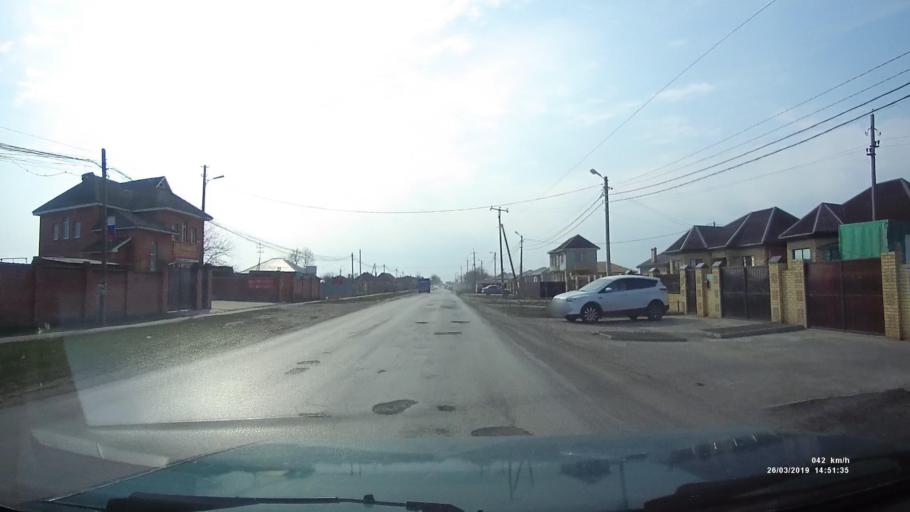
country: RU
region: Rostov
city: Novobessergenovka
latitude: 47.1840
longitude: 38.8275
